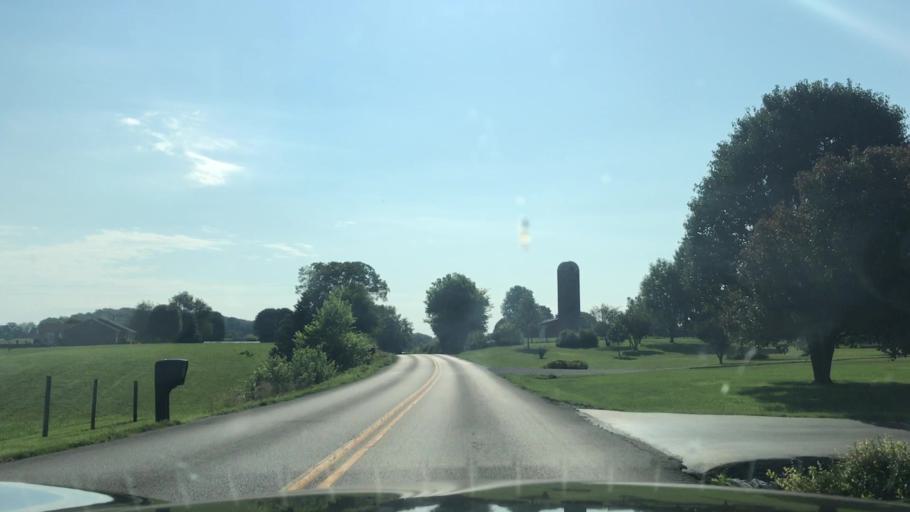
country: US
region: Kentucky
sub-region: Hart County
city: Horse Cave
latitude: 37.1664
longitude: -85.8324
